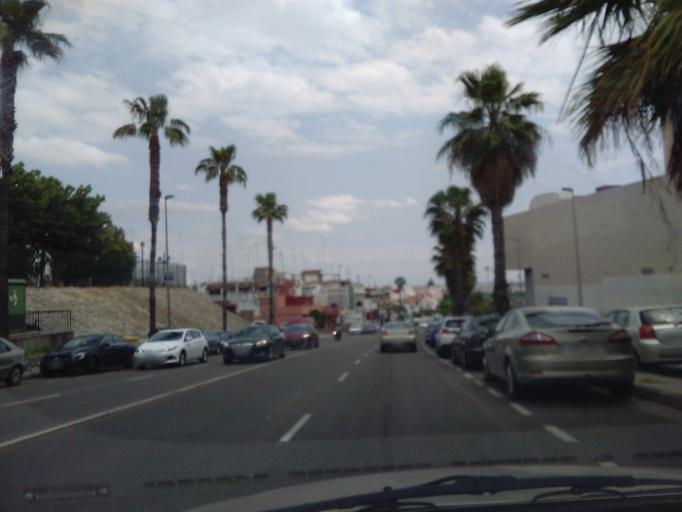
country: ES
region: Andalusia
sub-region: Provincia de Sevilla
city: Tomares
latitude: 37.3725
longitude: -6.0377
